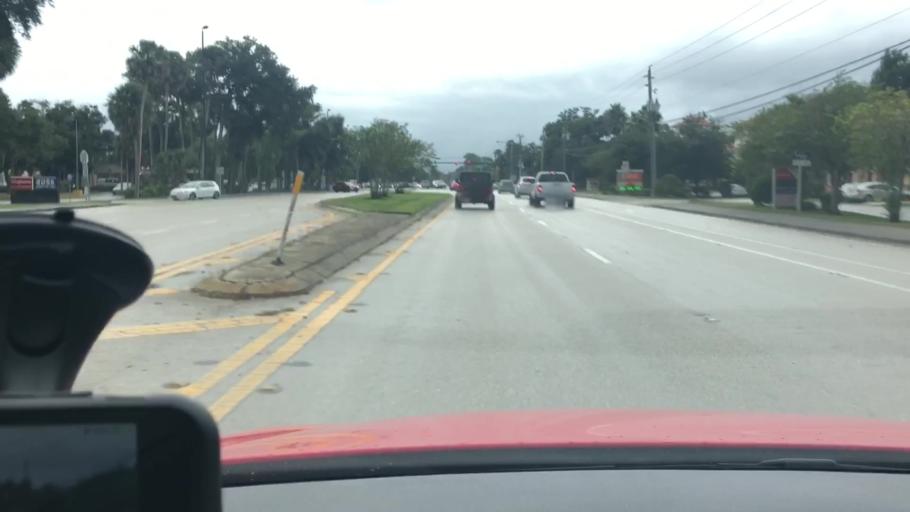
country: US
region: Florida
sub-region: Volusia County
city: Port Orange
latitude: 29.1295
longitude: -81.0062
